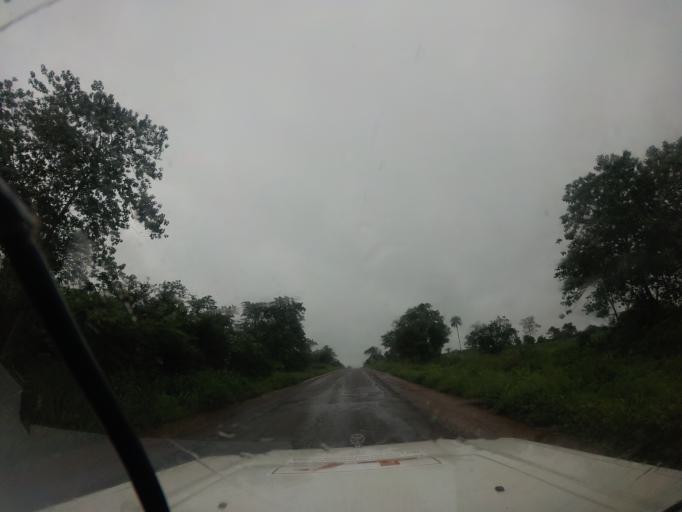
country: SL
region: Northern Province
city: Binkolo
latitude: 8.9321
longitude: -12.0037
